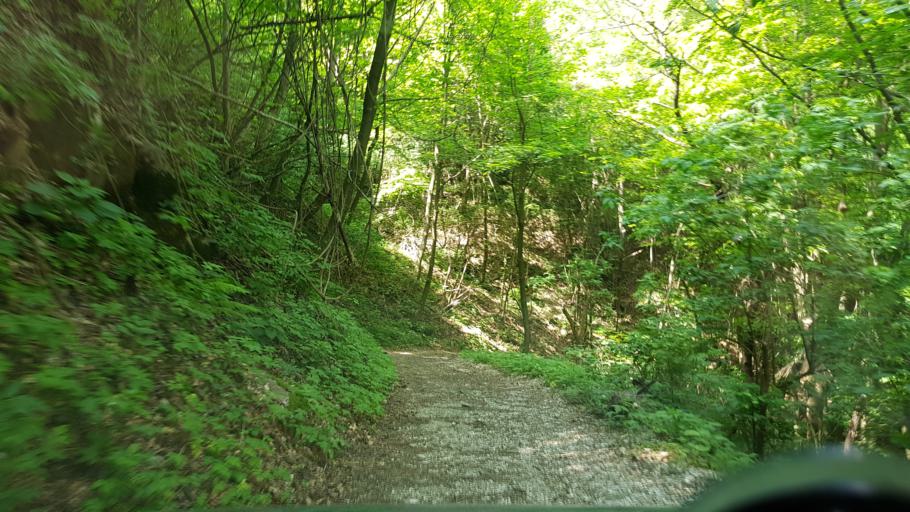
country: IT
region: Friuli Venezia Giulia
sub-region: Provincia di Udine
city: Pulfero
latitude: 46.1899
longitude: 13.4238
